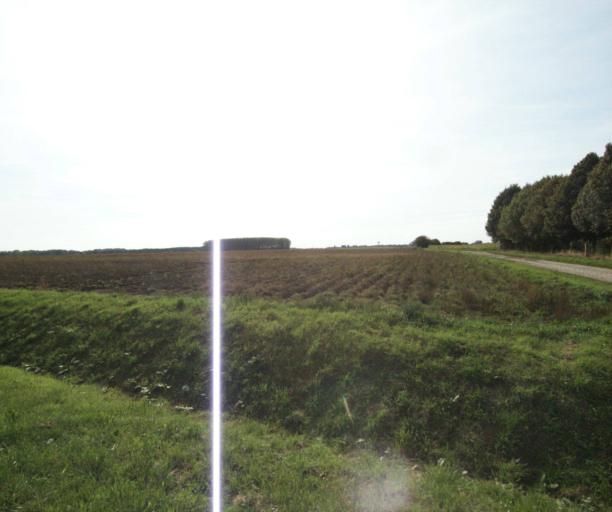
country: FR
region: Nord-Pas-de-Calais
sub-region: Departement du Nord
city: Wavrin
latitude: 50.5946
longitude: 2.9262
